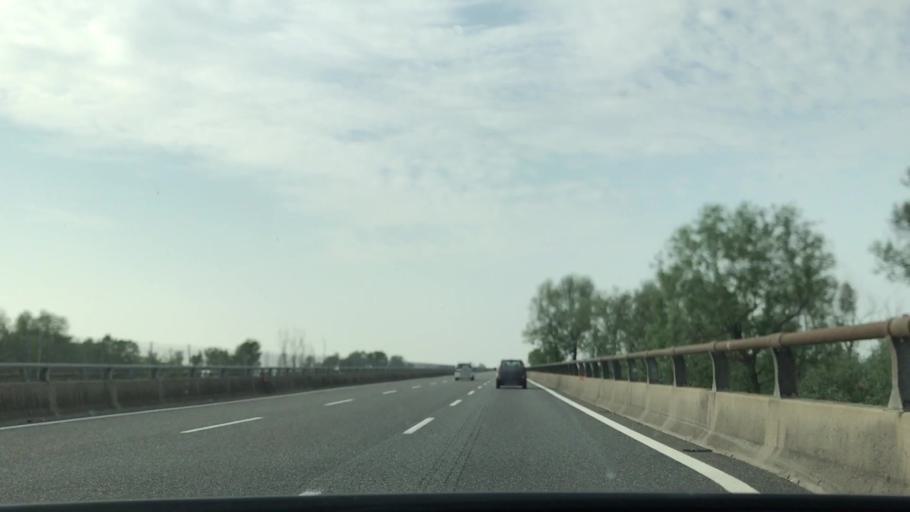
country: IT
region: Piedmont
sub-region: Provincia di Vercelli
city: Prarolo
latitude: 45.3058
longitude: 8.4705
